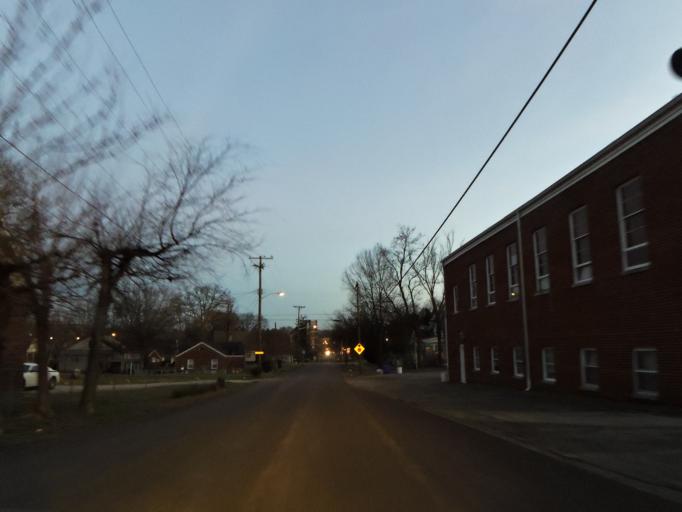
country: US
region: Tennessee
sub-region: Knox County
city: Knoxville
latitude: 35.9905
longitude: -83.8951
